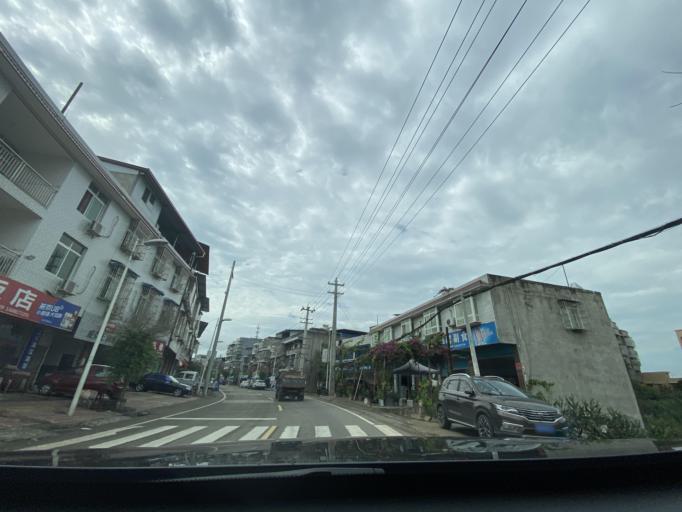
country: CN
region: Sichuan
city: Jiancheng
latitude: 30.4302
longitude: 104.6385
